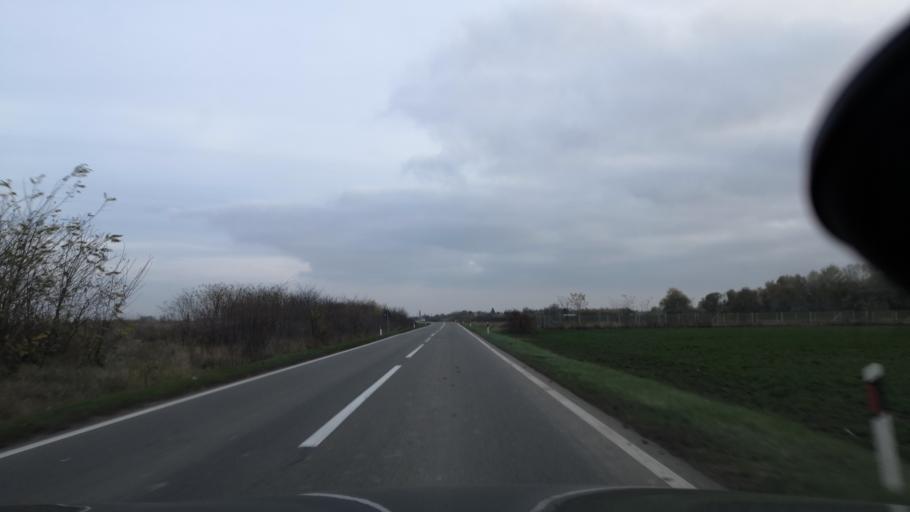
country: RS
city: Sanad
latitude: 45.9913
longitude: 20.1079
